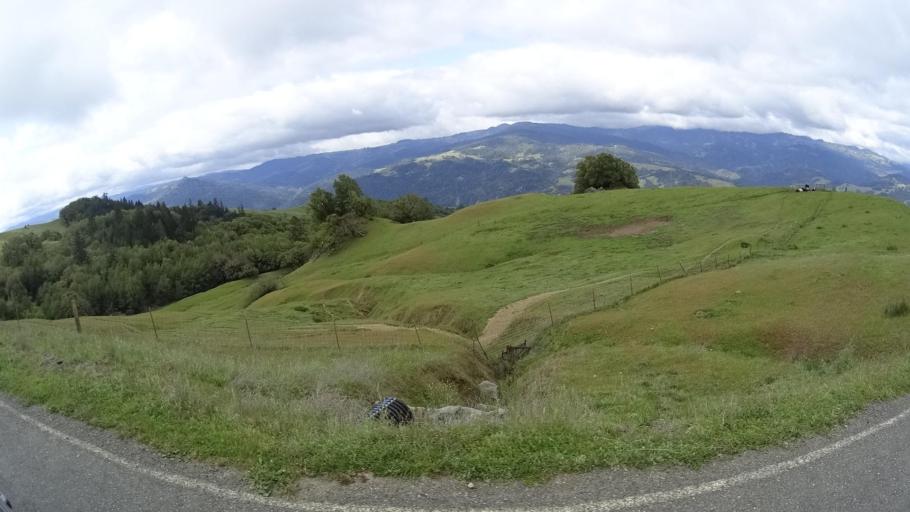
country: US
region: California
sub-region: Humboldt County
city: Redway
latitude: 40.1618
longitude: -123.5655
